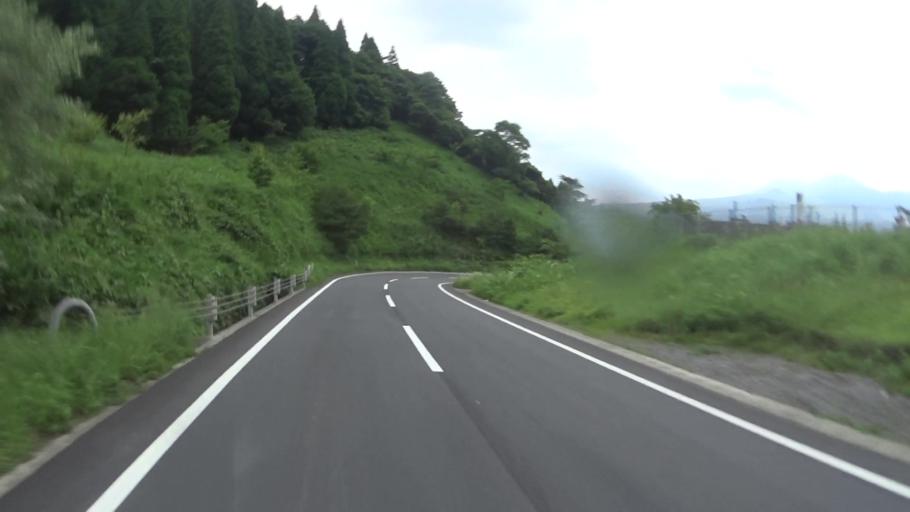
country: JP
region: Kumamoto
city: Aso
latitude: 32.9160
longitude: 130.9732
